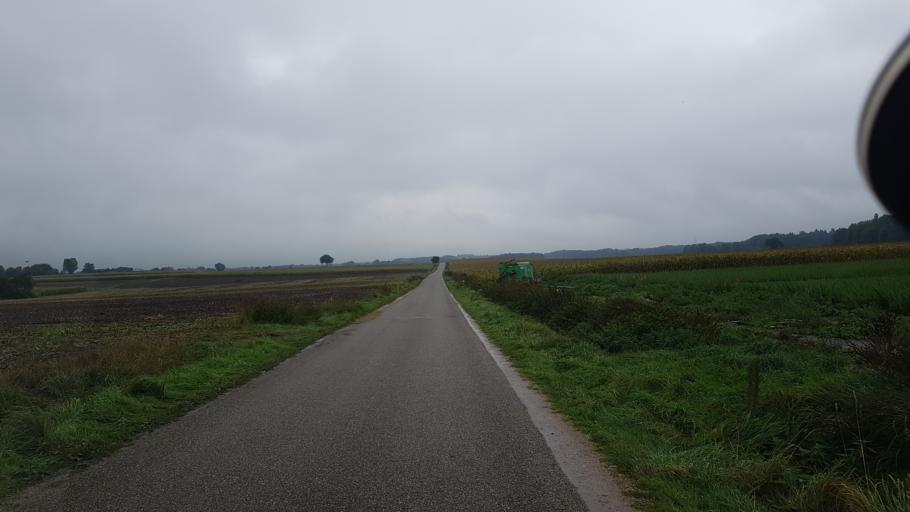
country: NL
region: Gelderland
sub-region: Gemeente Apeldoorn
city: Beekbergen
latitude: 52.1574
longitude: 5.9756
